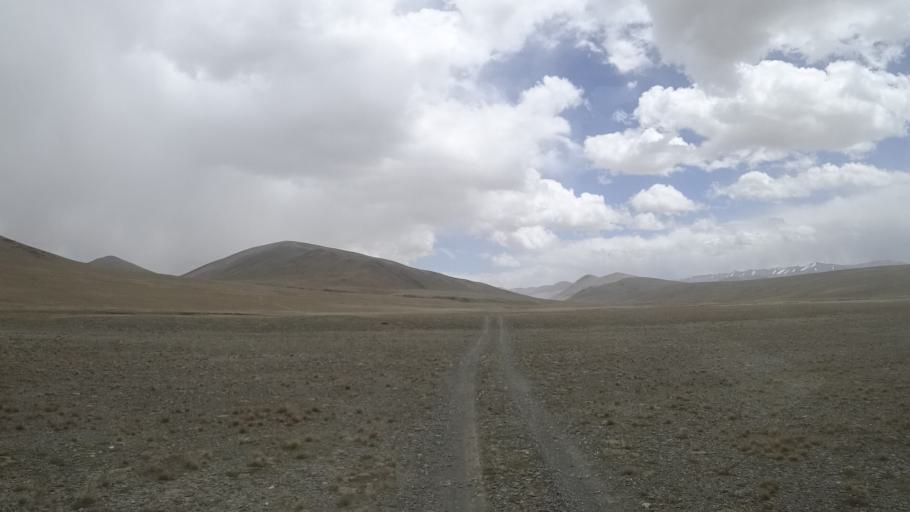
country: TJ
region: Gorno-Badakhshan
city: Murghob
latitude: 37.4910
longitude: 74.0290
